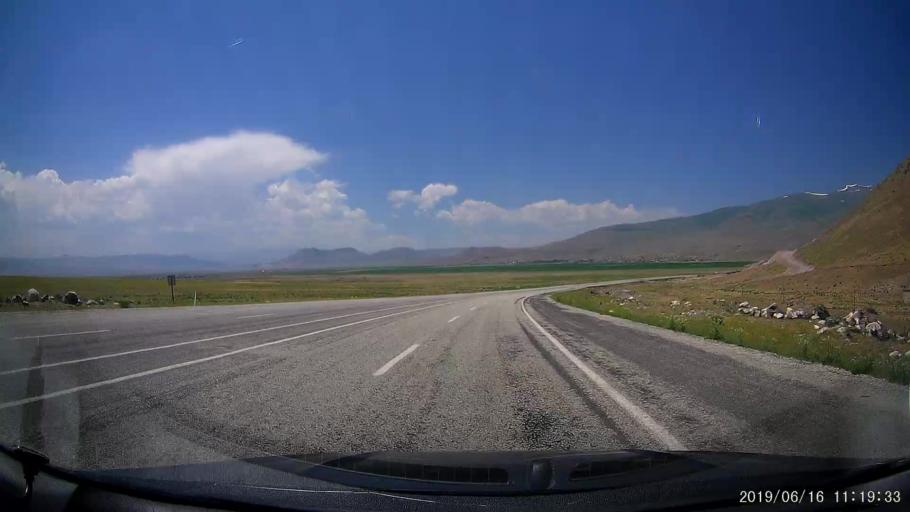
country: TR
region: Agri
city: Dogubayazit
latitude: 39.6974
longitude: 44.1121
